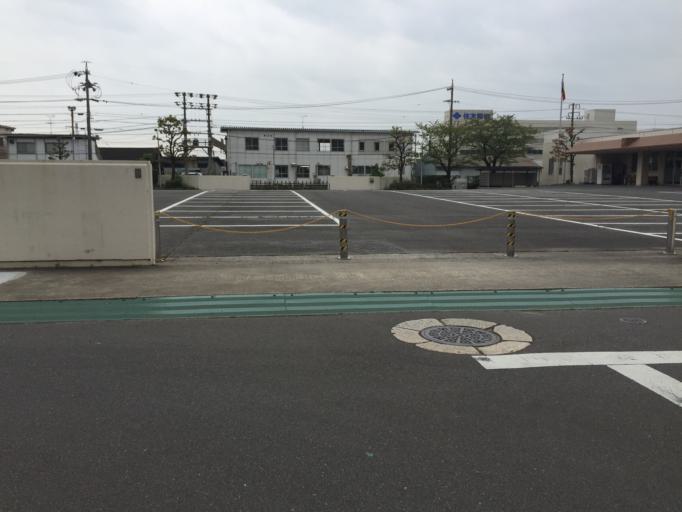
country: JP
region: Mie
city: Yokkaichi
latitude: 34.9619
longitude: 136.6283
